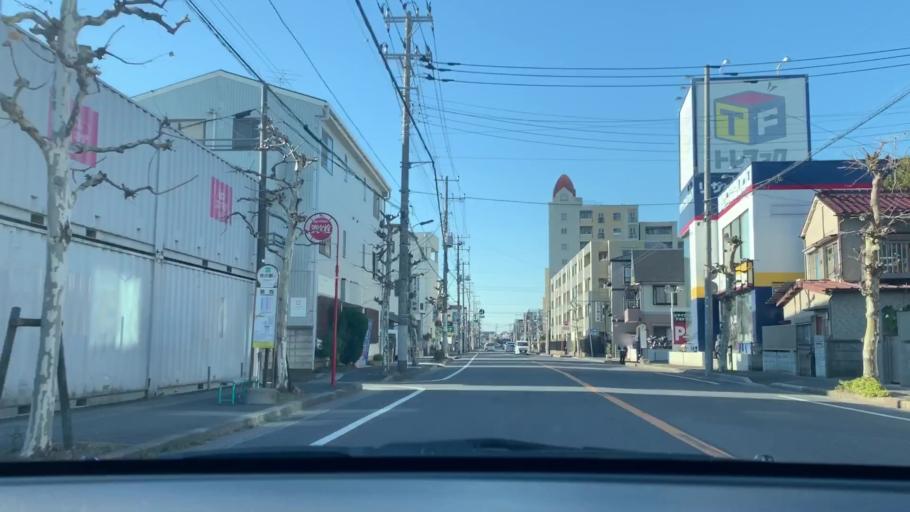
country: JP
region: Tokyo
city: Urayasu
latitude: 35.7148
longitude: 139.9163
